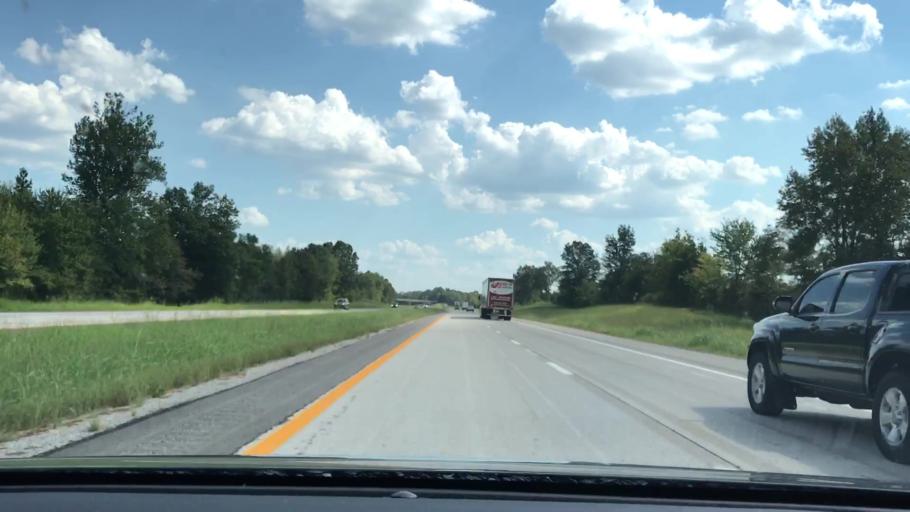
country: US
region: Kentucky
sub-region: Ohio County
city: Oak Grove
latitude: 37.3581
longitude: -86.7913
